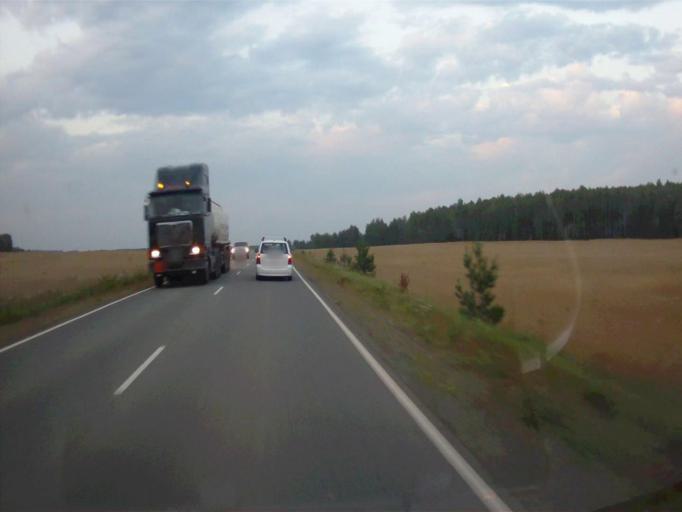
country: RU
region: Chelyabinsk
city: Chebarkul'
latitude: 55.1703
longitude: 60.4506
